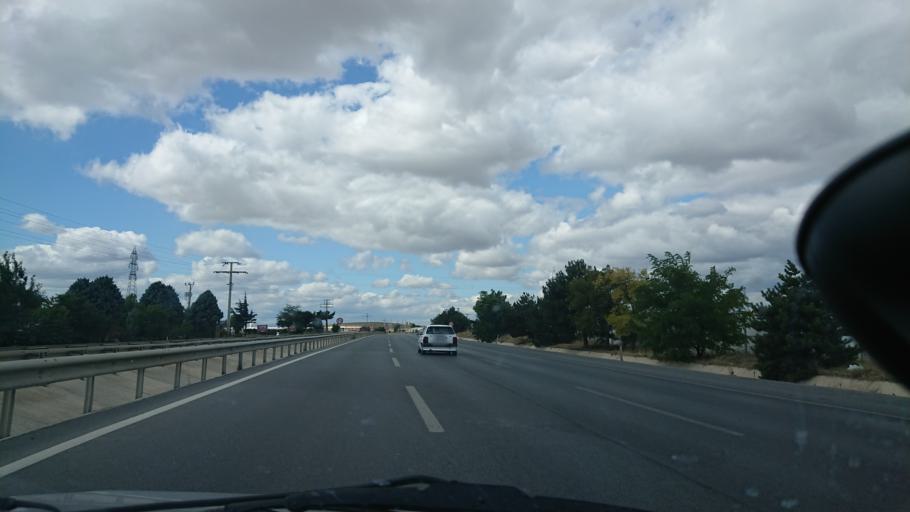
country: TR
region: Eskisehir
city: Eskisehir
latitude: 39.8142
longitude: 30.3800
